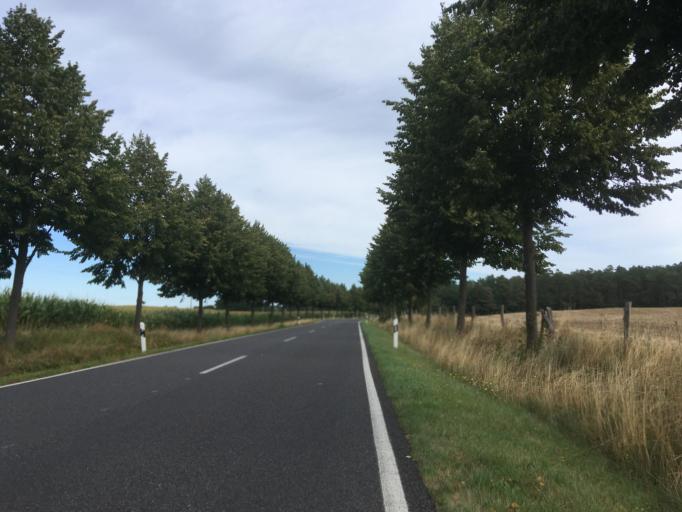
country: DE
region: Brandenburg
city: Templin
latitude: 53.1581
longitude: 13.5577
